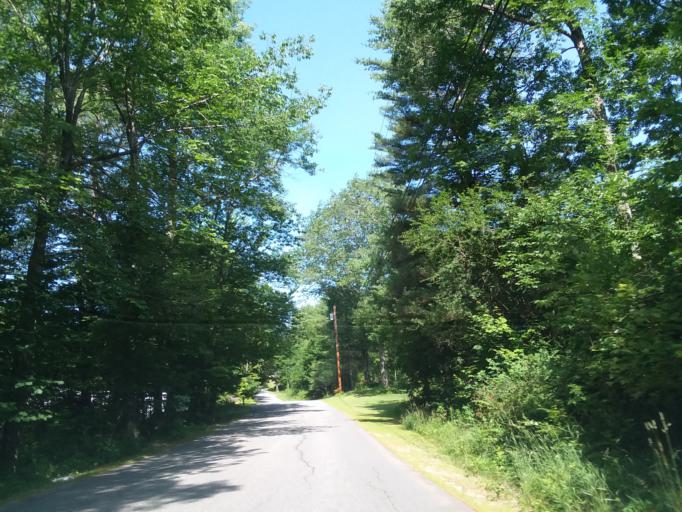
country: US
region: Maine
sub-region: Kennebec County
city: Monmouth
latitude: 44.2802
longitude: -70.0172
